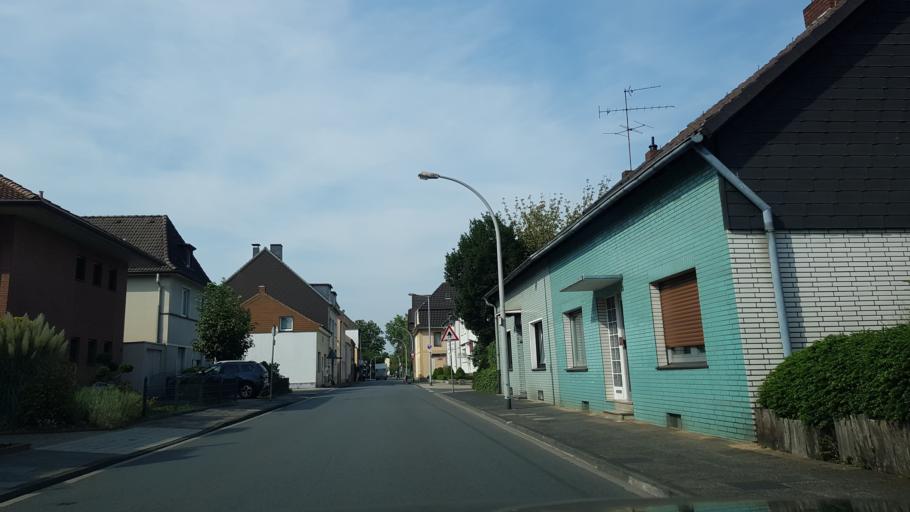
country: DE
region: North Rhine-Westphalia
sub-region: Regierungsbezirk Dusseldorf
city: Hochfeld
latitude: 51.3822
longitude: 6.7652
